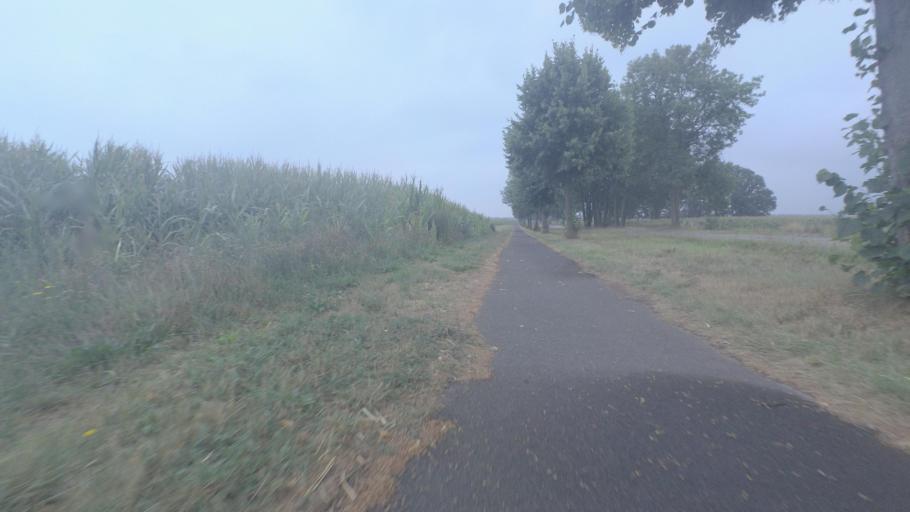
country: DE
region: Brandenburg
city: Heiligengrabe
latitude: 53.1431
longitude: 12.3660
